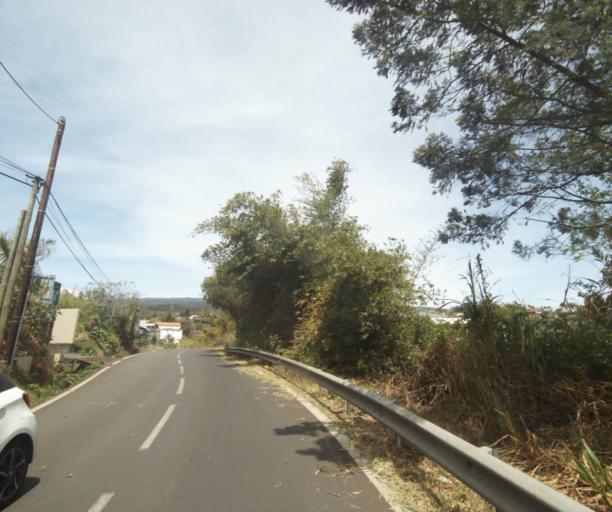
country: RE
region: Reunion
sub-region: Reunion
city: Saint-Paul
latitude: -21.0449
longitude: 55.3082
